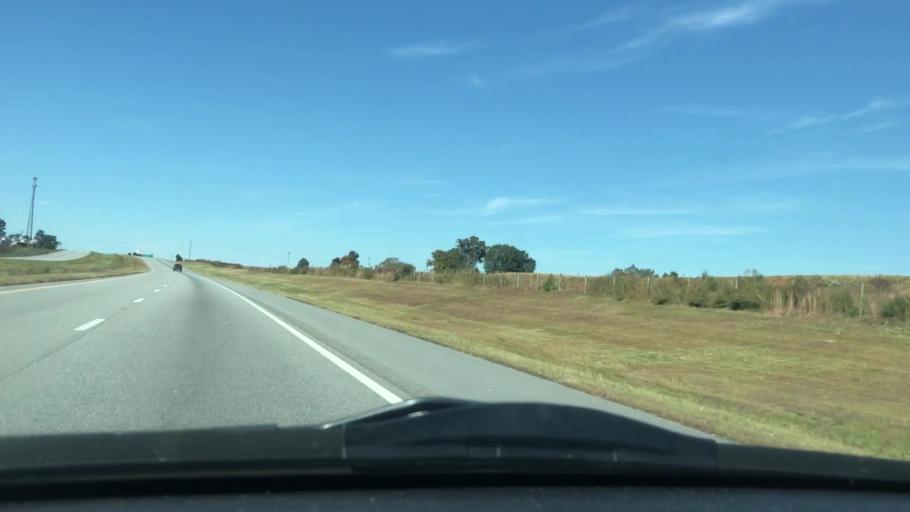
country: US
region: North Carolina
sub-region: Randolph County
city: Archdale
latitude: 35.8659
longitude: -79.8913
